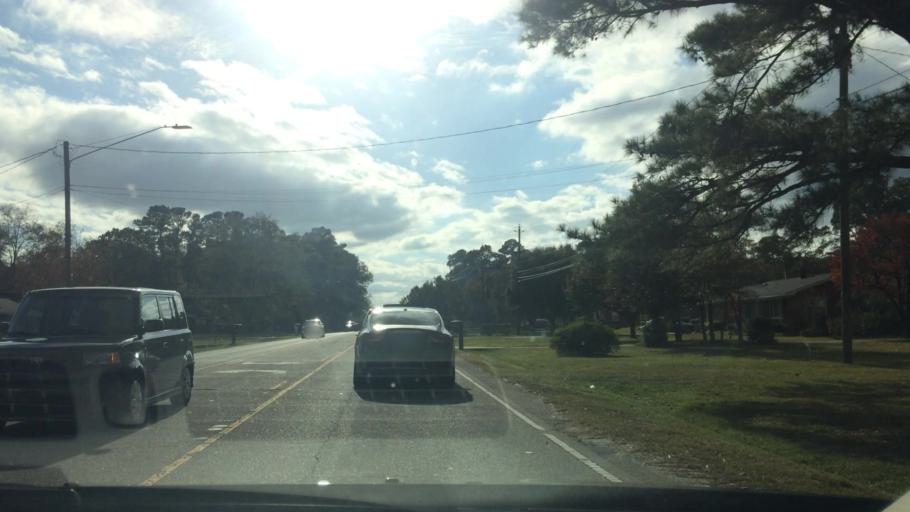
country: US
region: North Carolina
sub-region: Wayne County
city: Elroy
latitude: 35.3912
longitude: -77.9163
